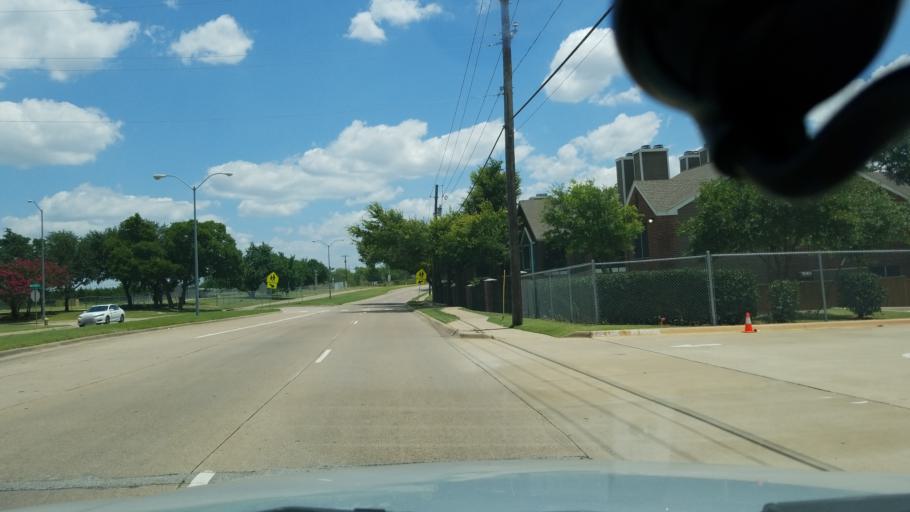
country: US
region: Texas
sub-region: Dallas County
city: Duncanville
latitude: 32.6766
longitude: -96.8817
